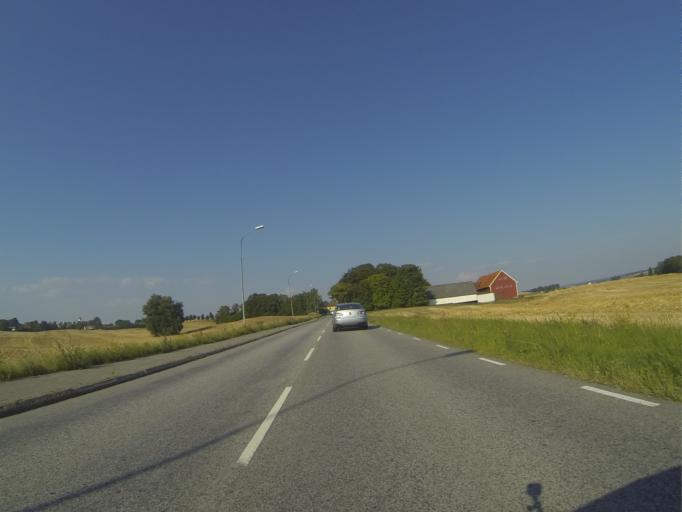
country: SE
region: Skane
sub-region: Svedala Kommun
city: Klagerup
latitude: 55.5818
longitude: 13.1981
